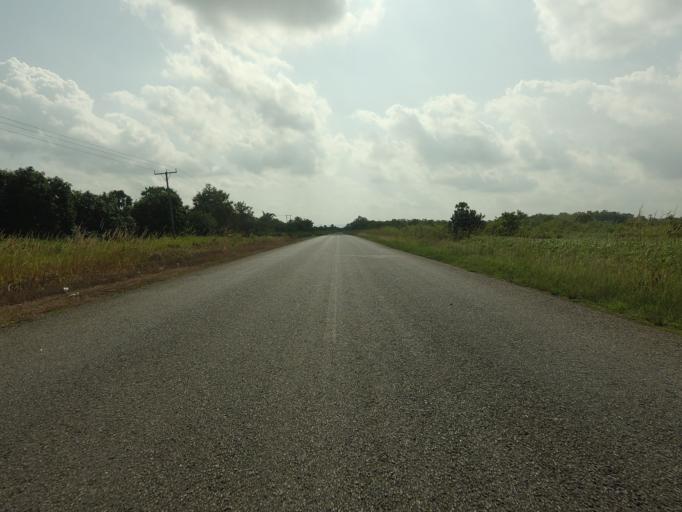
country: GH
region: Volta
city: Ho
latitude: 6.5810
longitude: 0.5782
